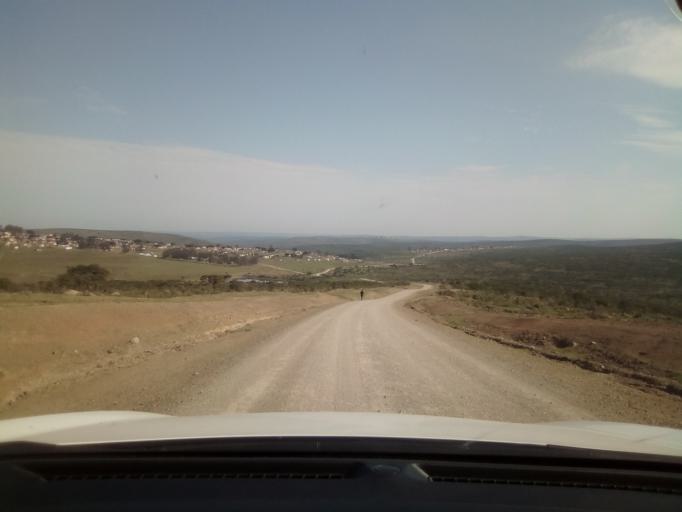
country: ZA
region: Eastern Cape
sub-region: Buffalo City Metropolitan Municipality
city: Bhisho
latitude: -32.9871
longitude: 27.2521
